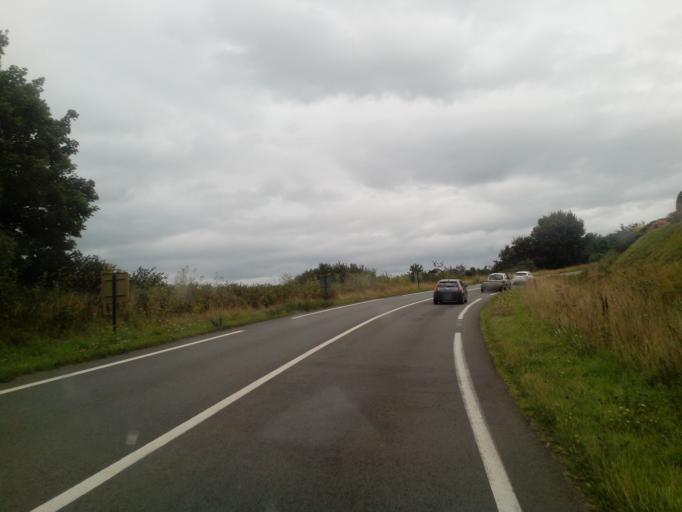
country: FR
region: Brittany
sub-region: Departement des Cotes-d'Armor
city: Etables-sur-Mer
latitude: 48.6352
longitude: -2.8271
